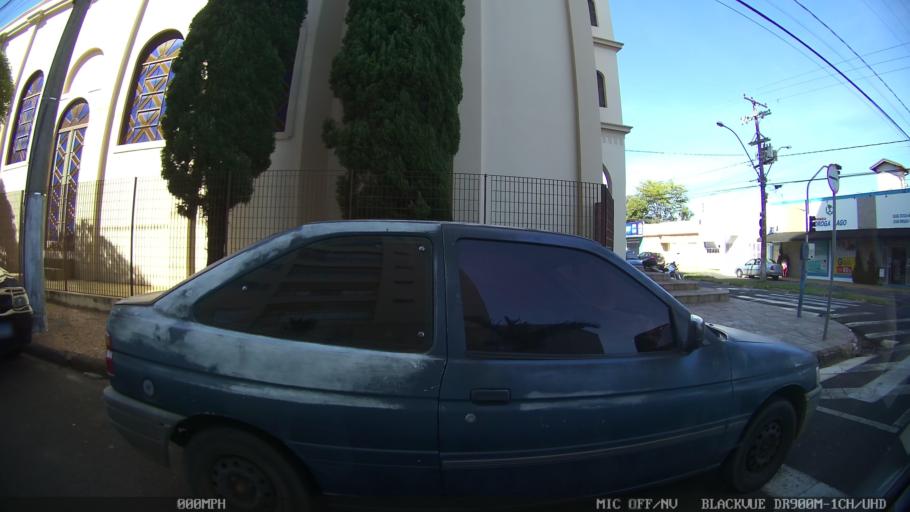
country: BR
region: Sao Paulo
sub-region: Franca
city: Franca
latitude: -20.5472
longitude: -47.3931
